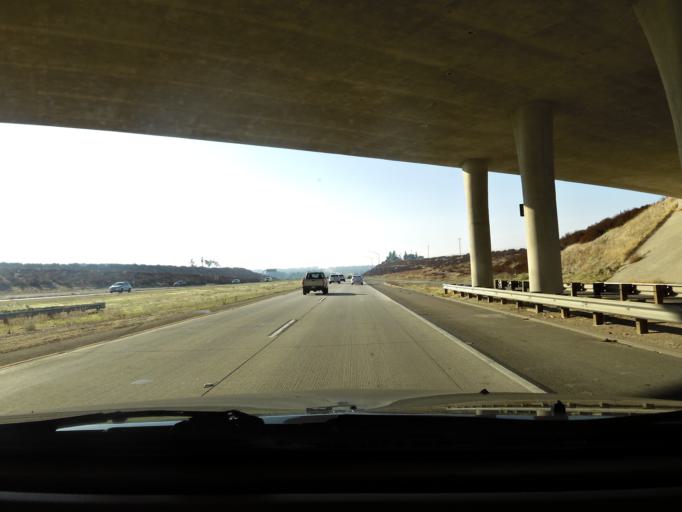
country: US
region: California
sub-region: Fresno County
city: Clovis
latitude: 36.8936
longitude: -119.7930
